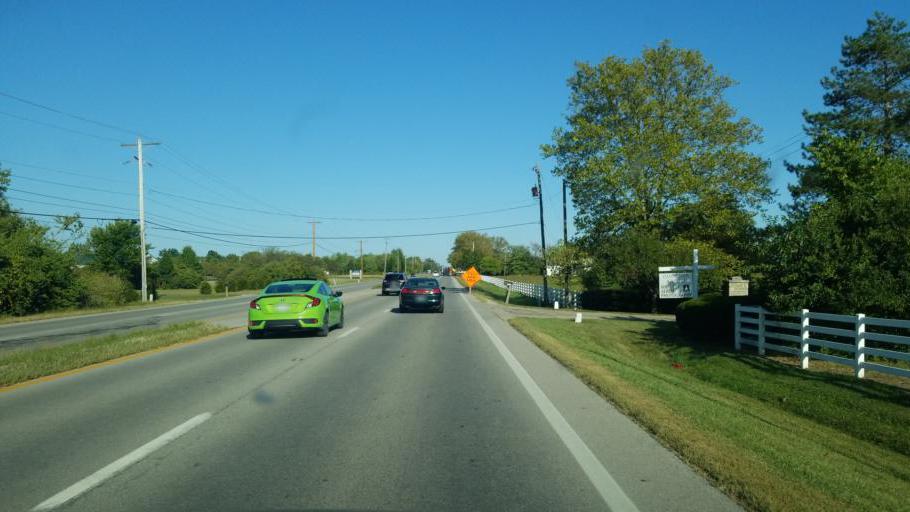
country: US
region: Ohio
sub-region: Franklin County
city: Lake Darby
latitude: 39.9489
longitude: -83.2036
